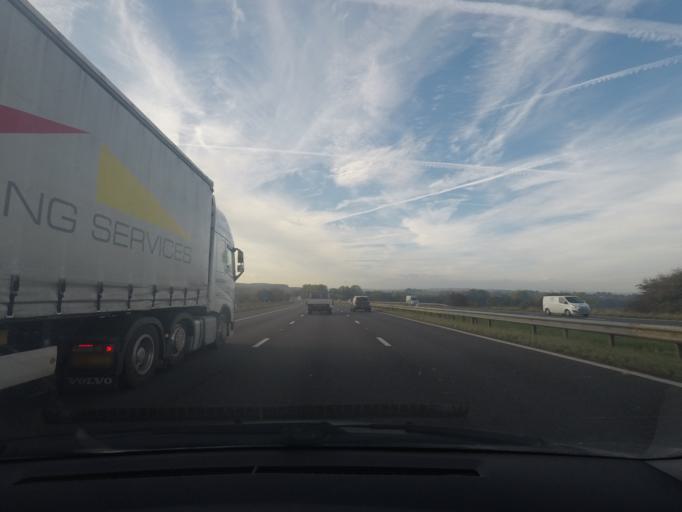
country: GB
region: England
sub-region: Barnsley
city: Darton
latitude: 53.5782
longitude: -1.5386
